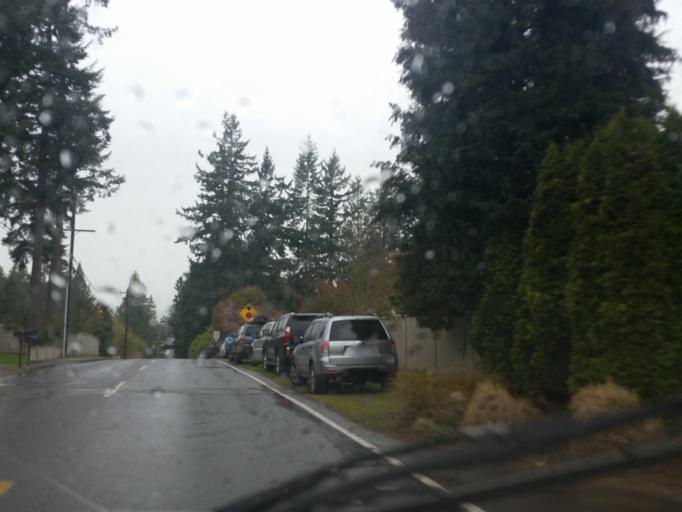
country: US
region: Washington
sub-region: Snohomish County
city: Edmonds
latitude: 47.8178
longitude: -122.3499
